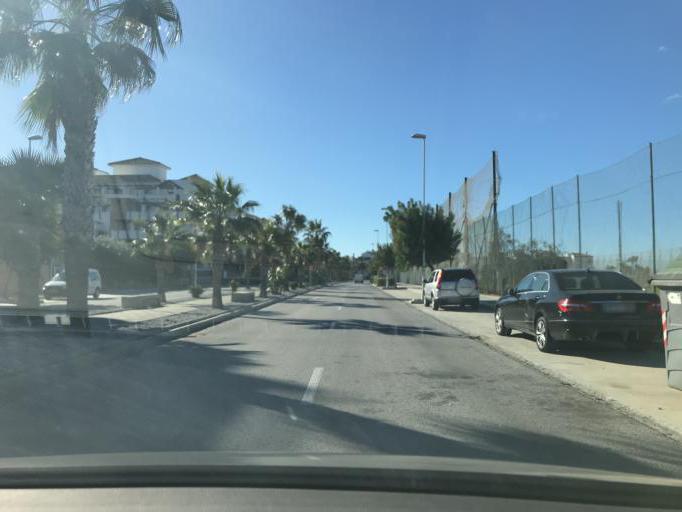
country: ES
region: Andalusia
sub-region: Provincia de Granada
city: Salobrena
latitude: 36.7227
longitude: -3.5596
